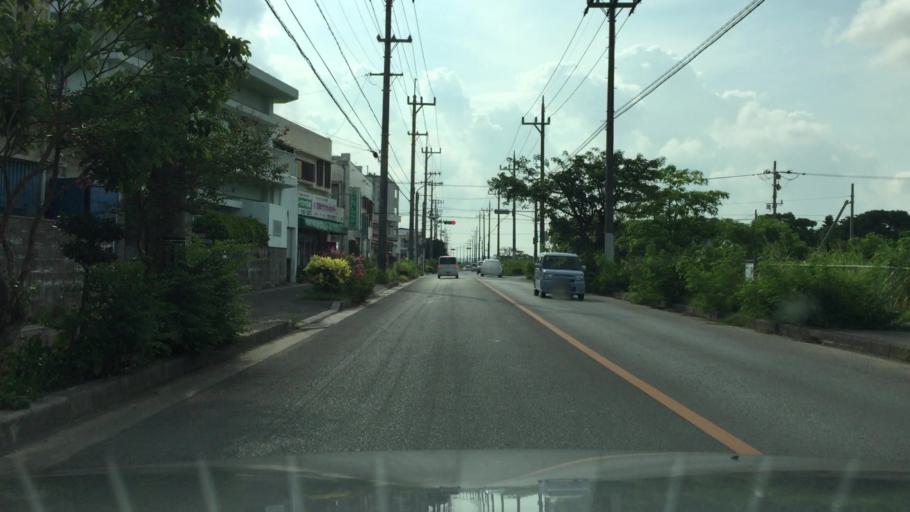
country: JP
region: Okinawa
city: Ishigaki
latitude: 24.3486
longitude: 124.1662
